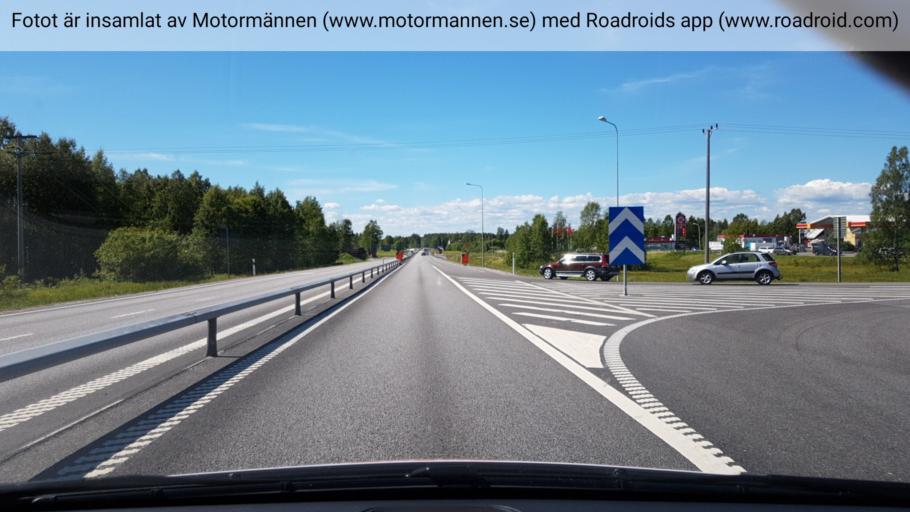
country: SE
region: Norrbotten
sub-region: Pitea Kommun
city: Norrfjarden
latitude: 65.4102
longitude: 21.5094
